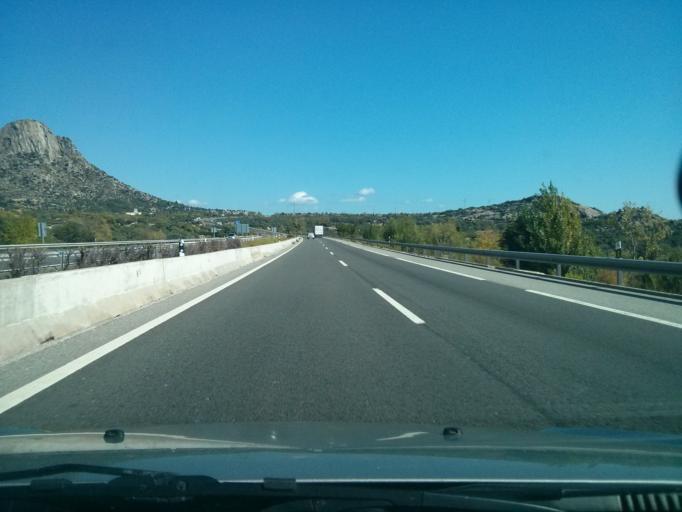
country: ES
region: Madrid
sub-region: Provincia de Madrid
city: La Cabrera
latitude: 40.8582
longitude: -3.6089
